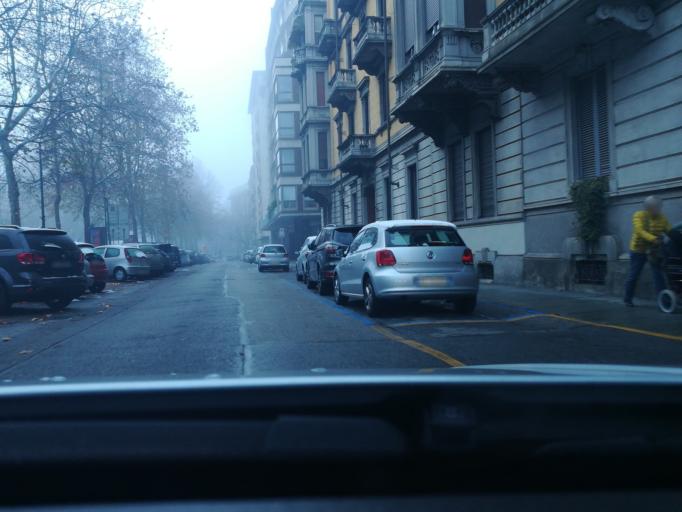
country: IT
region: Piedmont
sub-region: Provincia di Torino
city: Turin
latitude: 45.0481
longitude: 7.6794
